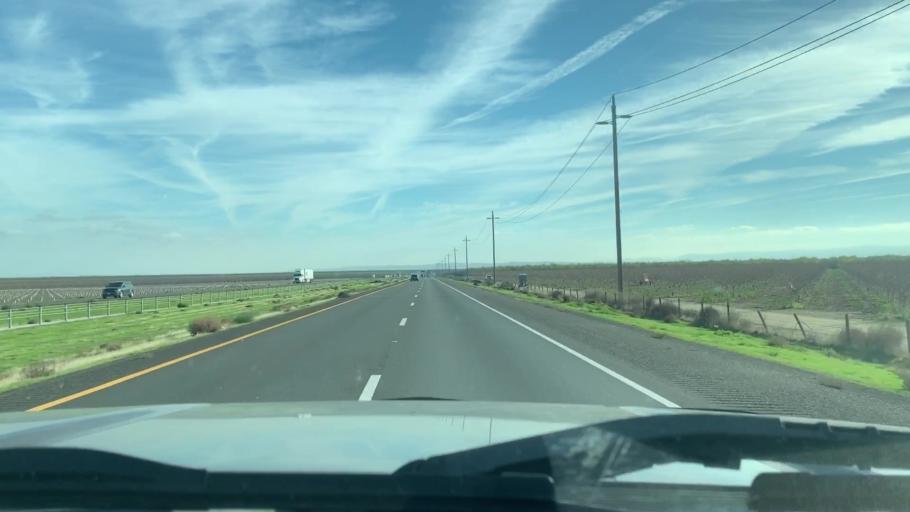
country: US
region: California
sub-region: Fresno County
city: Huron
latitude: 36.2394
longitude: -120.2348
